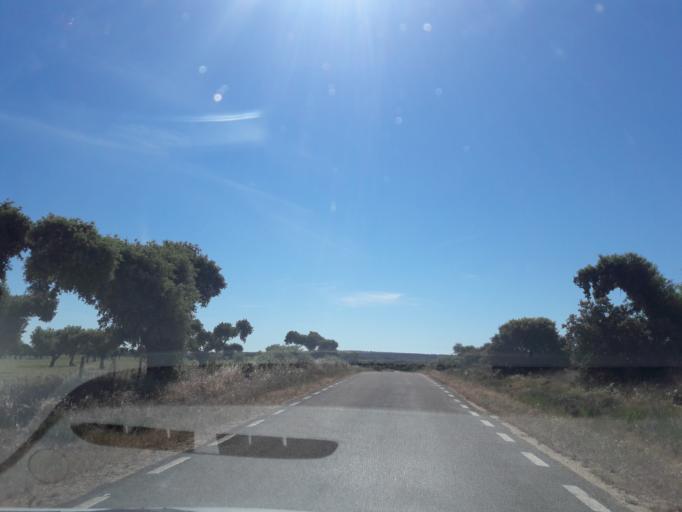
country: ES
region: Castille and Leon
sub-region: Provincia de Salamanca
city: Zarapicos
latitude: 41.0238
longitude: -5.8322
